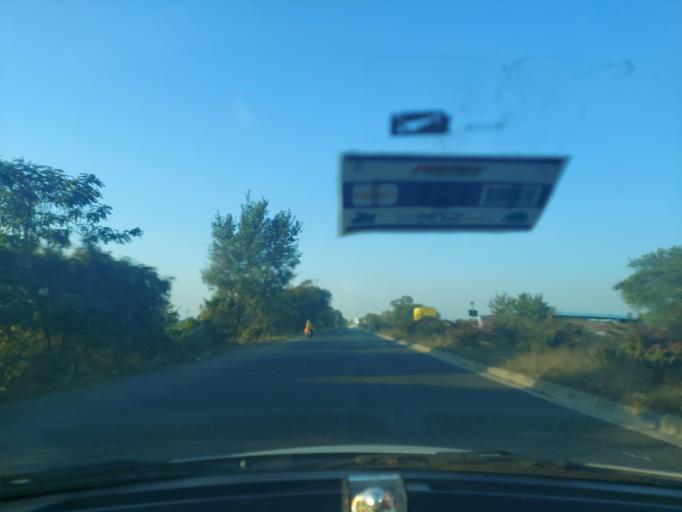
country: IN
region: Madhya Pradesh
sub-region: Indore
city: Sanwer
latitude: 23.0629
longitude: 75.8231
